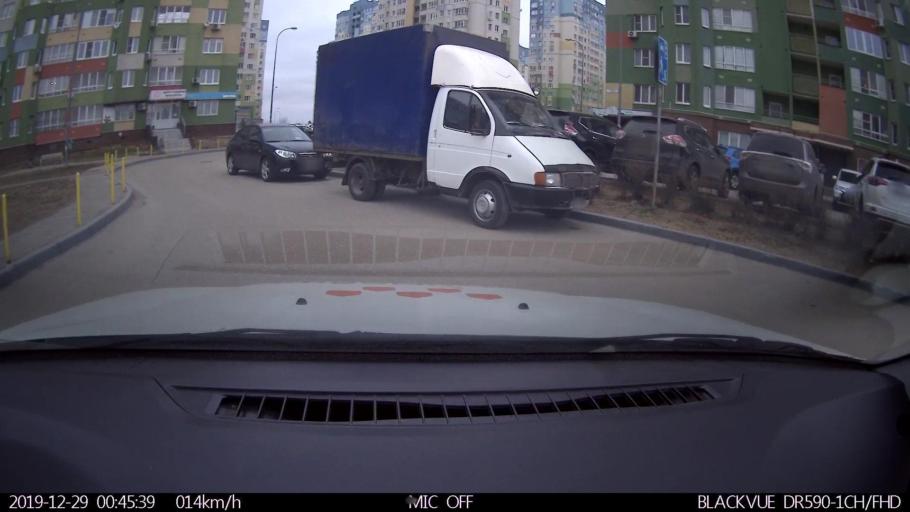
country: RU
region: Nizjnij Novgorod
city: Nizhniy Novgorod
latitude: 56.3402
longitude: 43.9495
